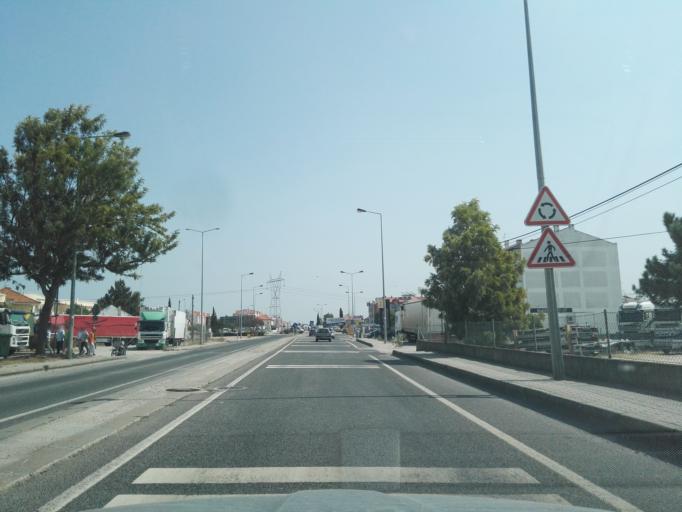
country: PT
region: Santarem
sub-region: Benavente
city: Samora Correia
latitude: 38.9222
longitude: -8.8836
